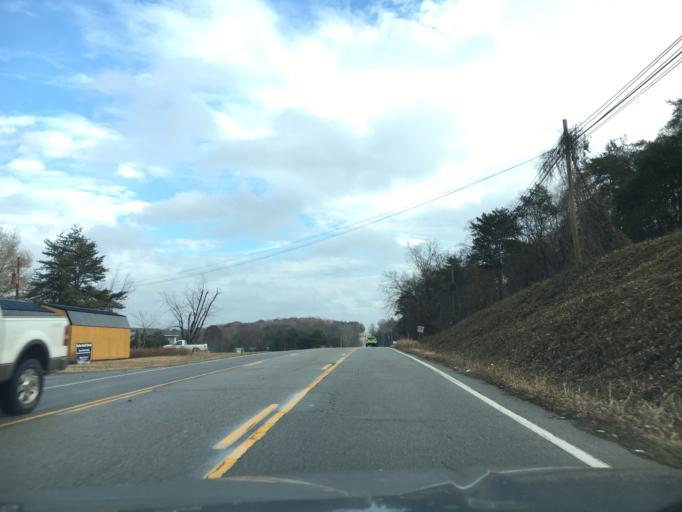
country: US
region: Virginia
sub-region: Prince Edward County
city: Farmville
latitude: 37.3160
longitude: -78.4529
